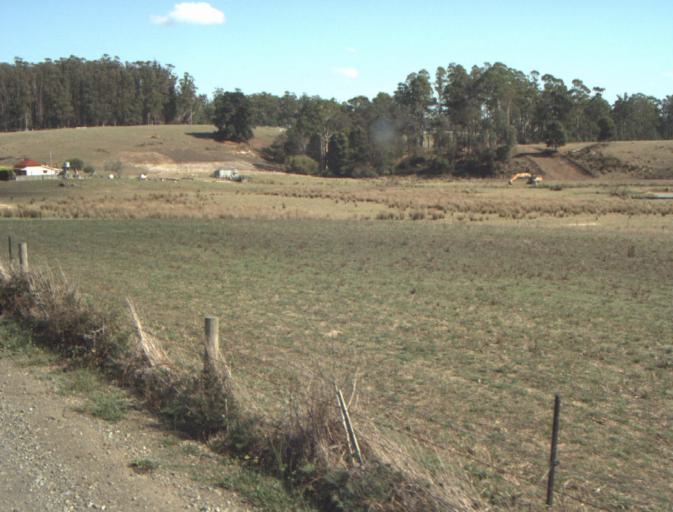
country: AU
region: Tasmania
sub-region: Launceston
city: Mayfield
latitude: -41.2243
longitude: 147.2370
